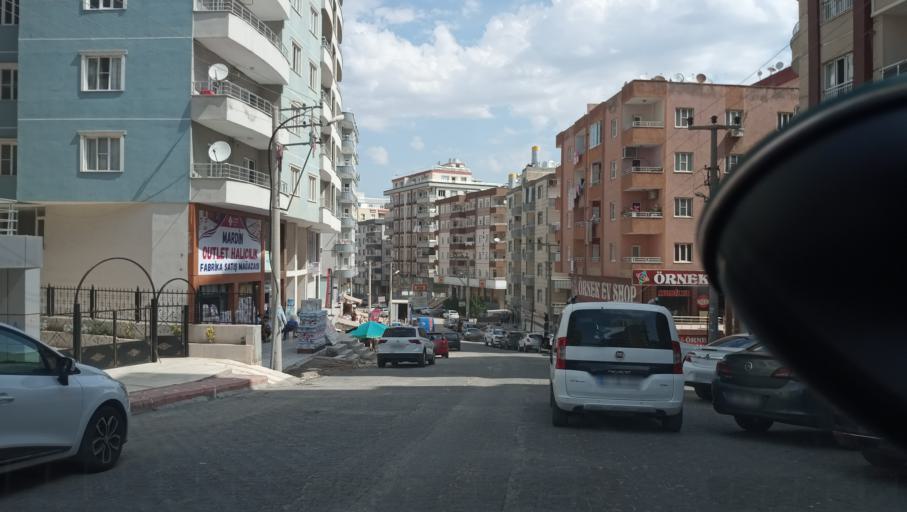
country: TR
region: Mardin
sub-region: Mardin Ilcesi
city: Mardin
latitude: 37.3268
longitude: 40.7176
